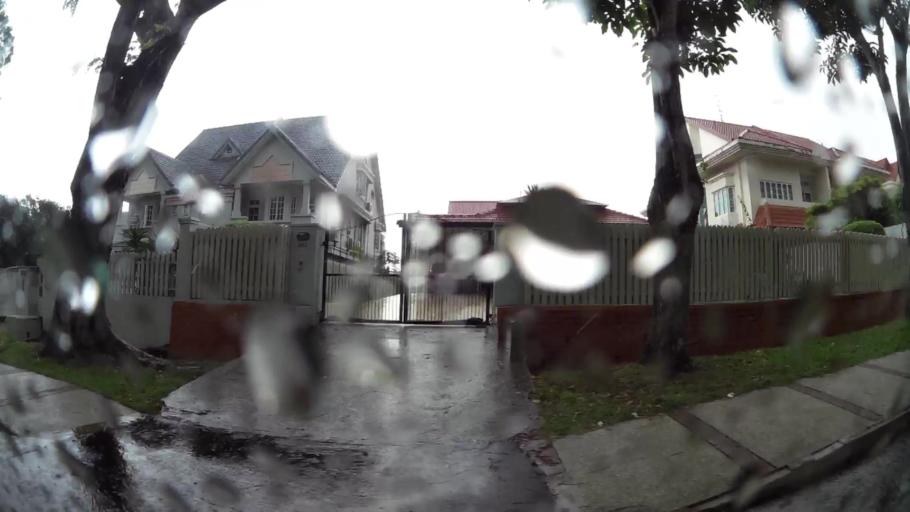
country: SG
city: Singapore
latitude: 1.3302
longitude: 103.9484
